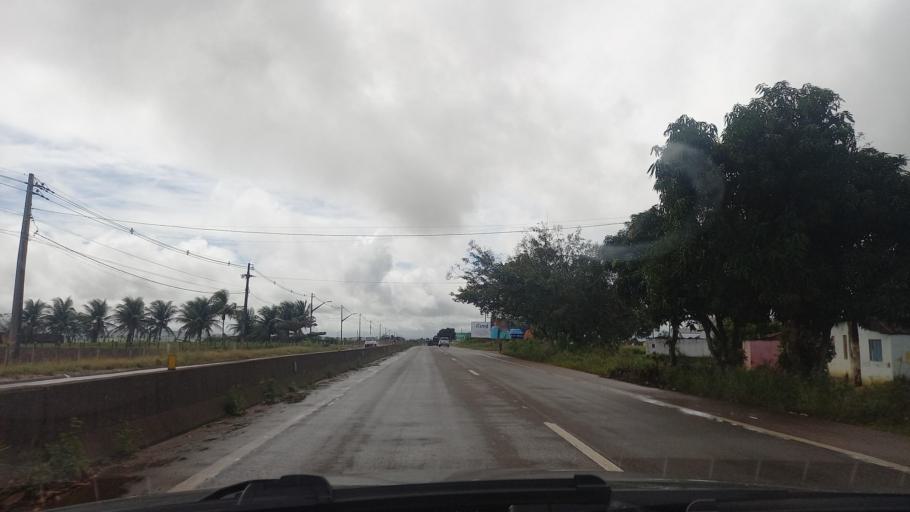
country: BR
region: Alagoas
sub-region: Limoeiro De Anadia
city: Limoeiro de Anadia
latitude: -9.7620
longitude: -36.5305
